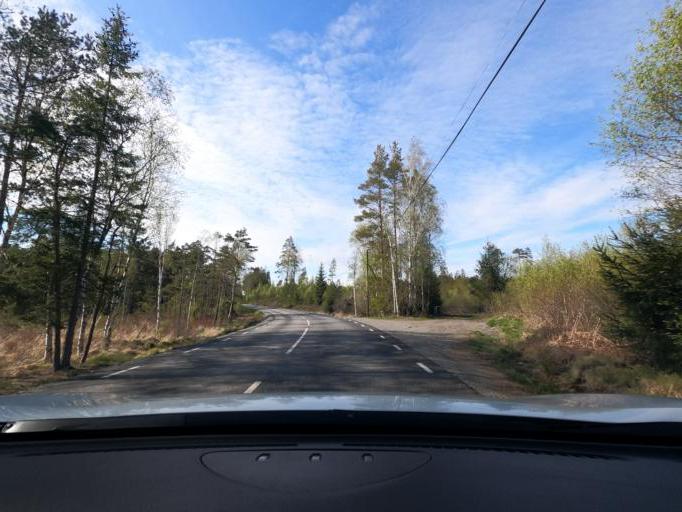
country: SE
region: Vaestra Goetaland
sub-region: Harryda Kommun
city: Landvetter
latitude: 57.6577
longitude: 12.2663
